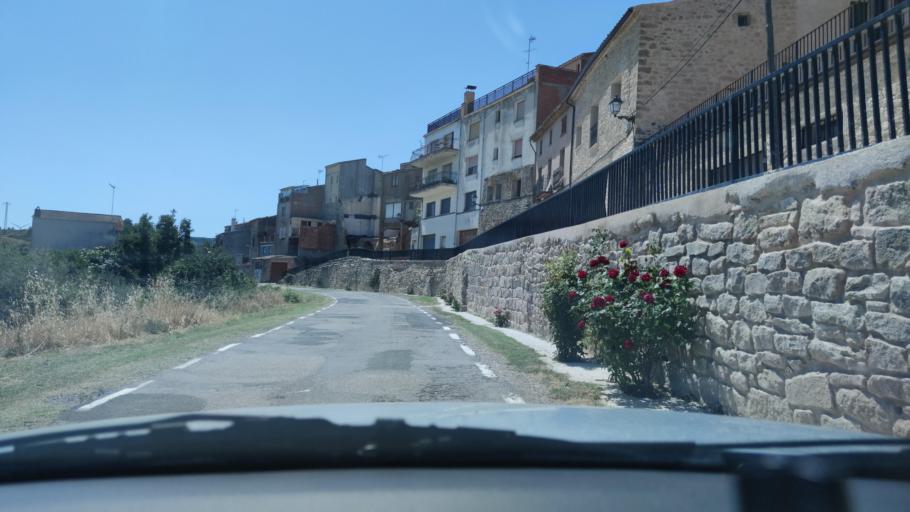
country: ES
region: Catalonia
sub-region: Provincia de Lleida
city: Fulleda
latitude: 41.4643
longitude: 1.0244
